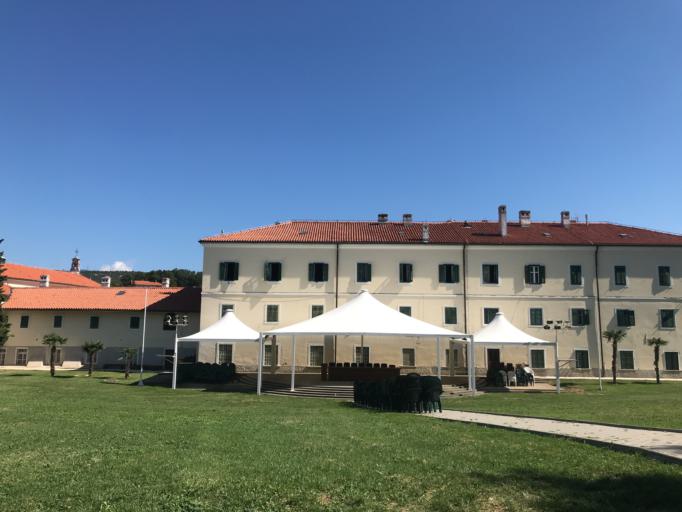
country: HR
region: Primorsko-Goranska
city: Drenova
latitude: 45.3304
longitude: 14.4567
